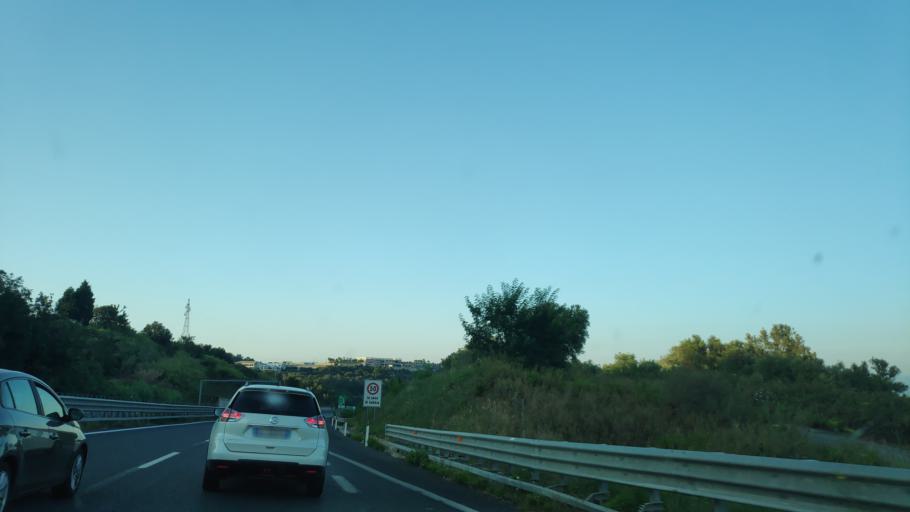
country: IT
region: Calabria
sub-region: Provincia di Reggio Calabria
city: Seminara
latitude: 38.3700
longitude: 15.8665
